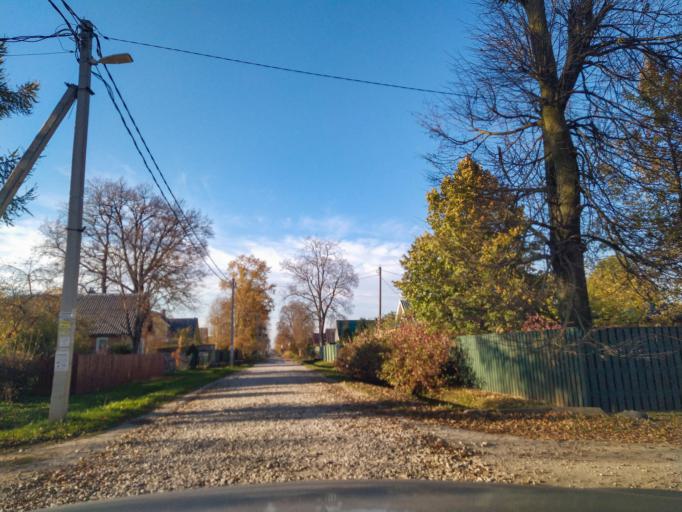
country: RU
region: Leningrad
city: Siverskiy
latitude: 59.3254
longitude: 30.0423
